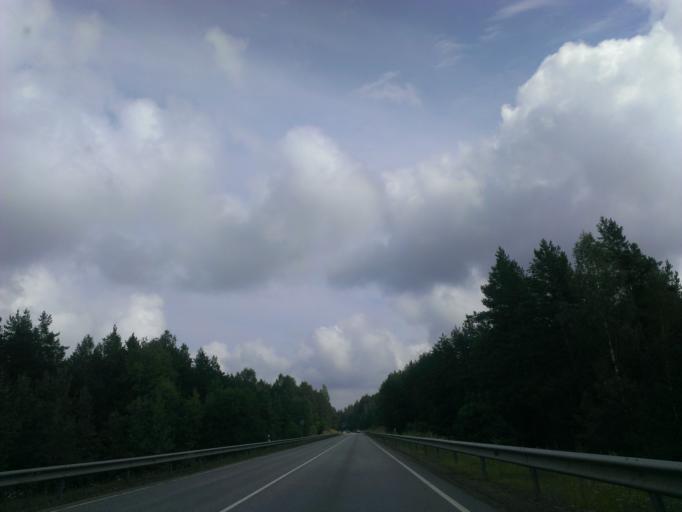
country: LV
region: Sigulda
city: Sigulda
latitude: 57.1339
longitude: 24.7865
